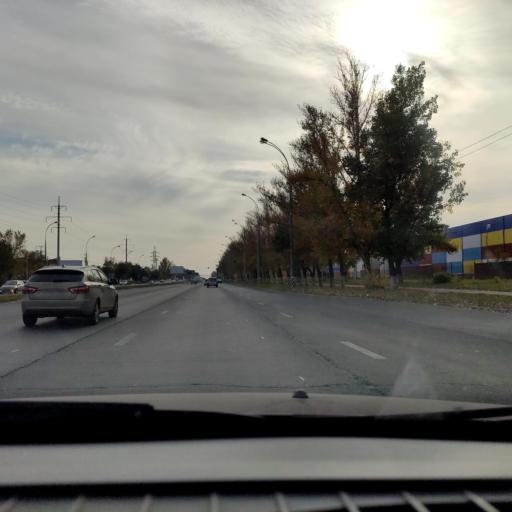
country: RU
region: Samara
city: Tol'yatti
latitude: 53.5494
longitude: 49.2865
